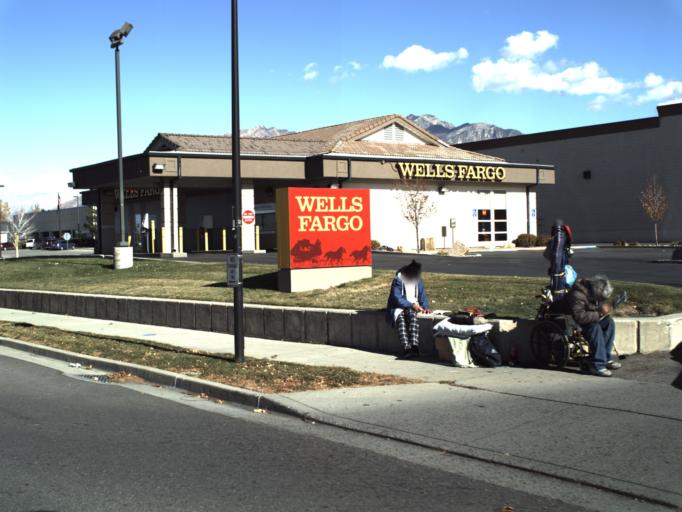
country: US
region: Utah
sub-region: Salt Lake County
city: Sandy Hills
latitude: 40.5816
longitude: -111.8339
